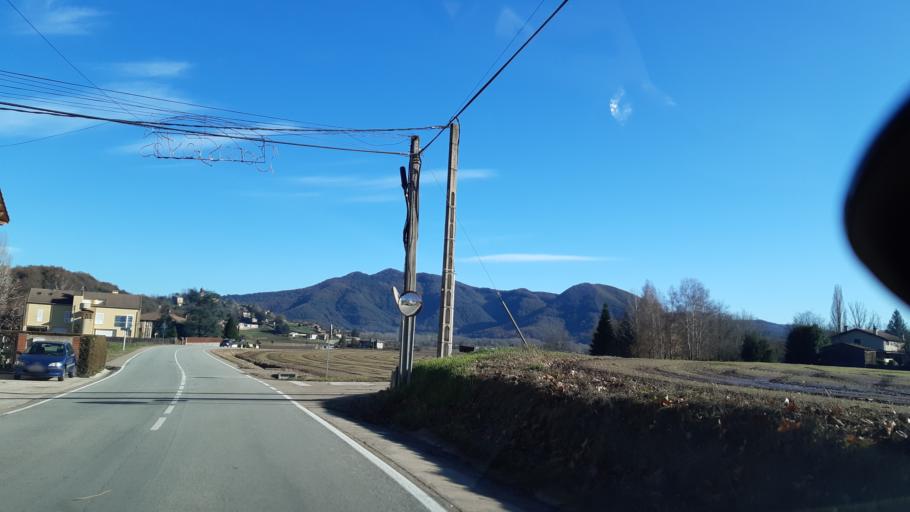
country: ES
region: Catalonia
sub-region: Provincia de Girona
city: Bas
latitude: 42.1500
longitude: 2.4246
